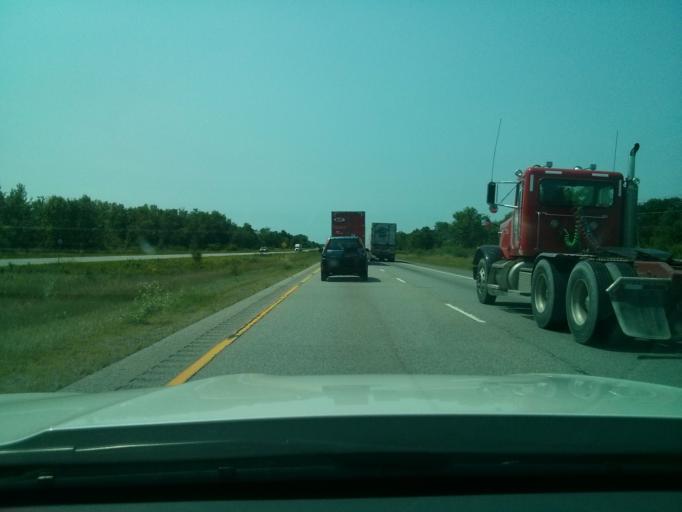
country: CA
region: Ontario
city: Prescott
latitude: 44.6814
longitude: -75.5923
